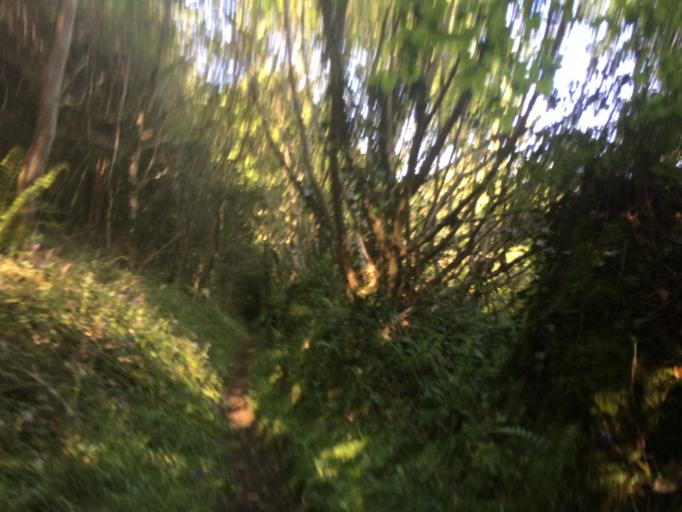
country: FR
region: Brittany
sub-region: Departement du Finistere
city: Daoulas
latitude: 48.3518
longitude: -4.2476
